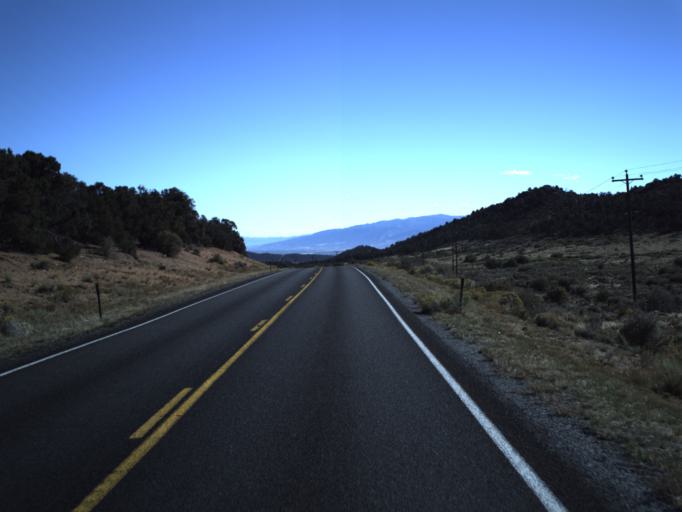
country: US
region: Utah
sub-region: Iron County
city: Cedar City
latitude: 37.6139
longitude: -113.3405
